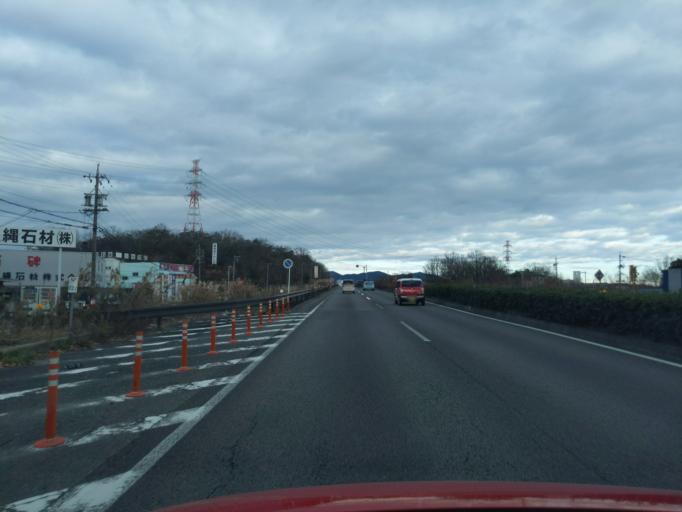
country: JP
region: Aichi
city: Kasugai
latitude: 35.2763
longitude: 137.0087
